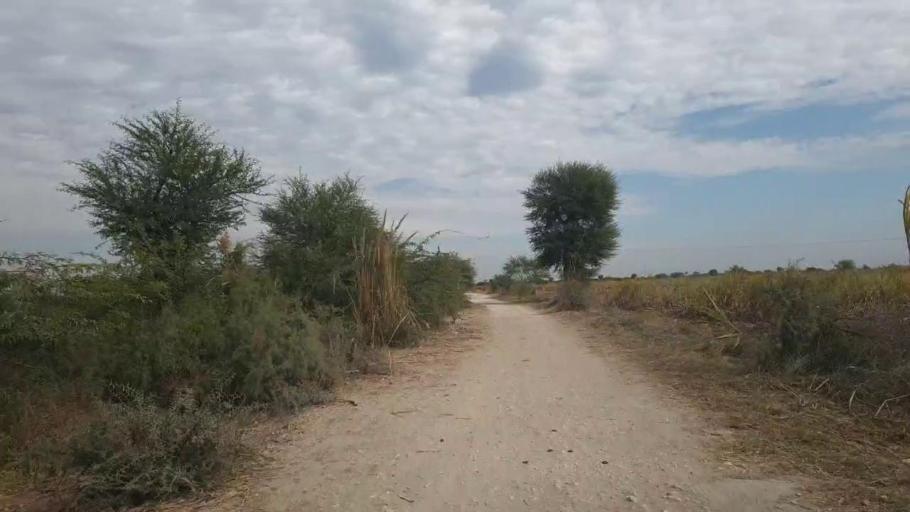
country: PK
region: Sindh
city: Jhol
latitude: 26.0144
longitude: 68.8736
